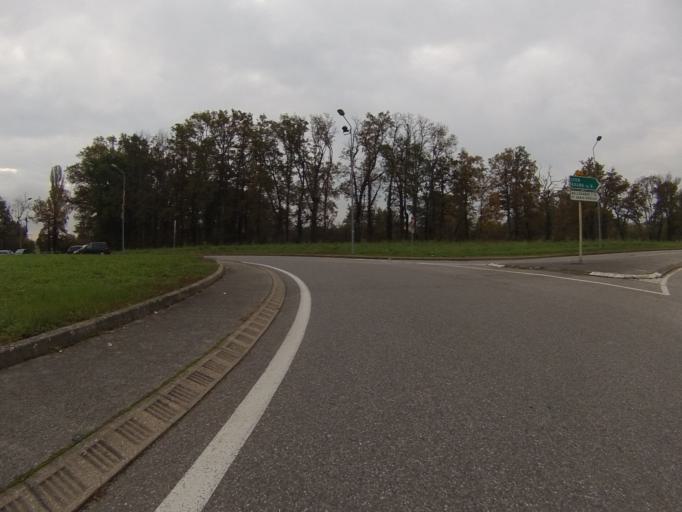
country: CH
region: Geneva
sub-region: Geneva
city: Meyrin
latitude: 46.2462
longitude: 6.0811
